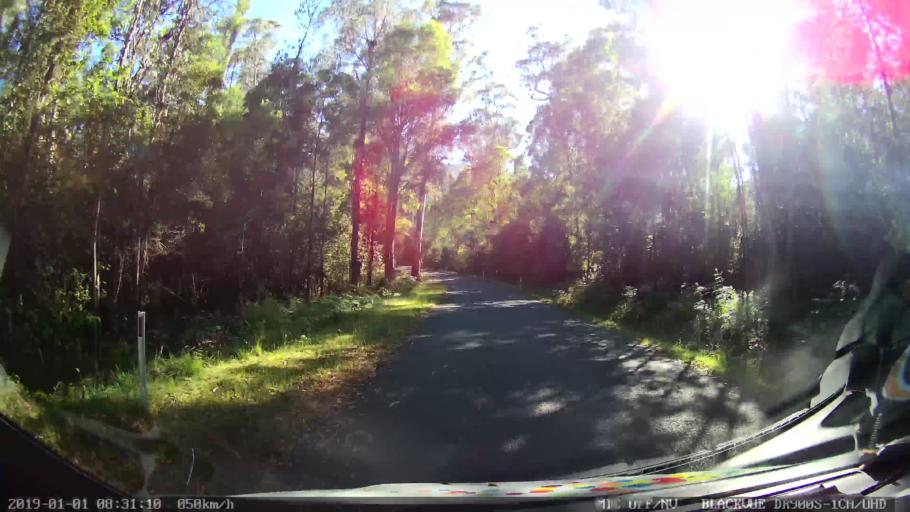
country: AU
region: New South Wales
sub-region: Snowy River
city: Jindabyne
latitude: -36.3720
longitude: 148.2037
